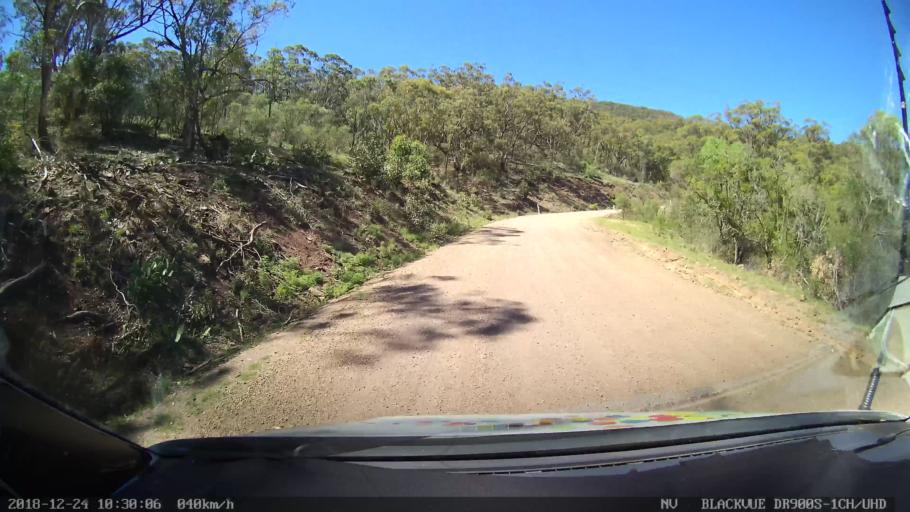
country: AU
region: New South Wales
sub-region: Upper Hunter Shire
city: Merriwa
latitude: -31.8352
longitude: 150.5266
